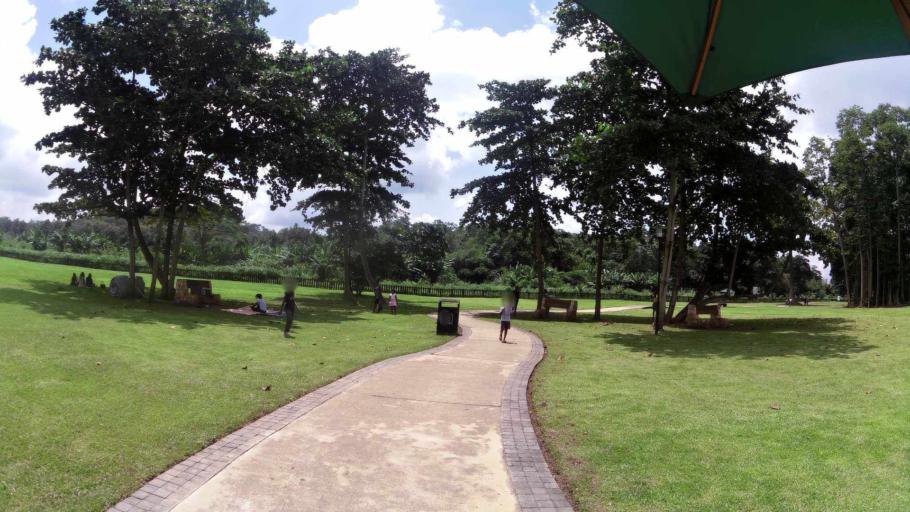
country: NG
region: Oyo
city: Ibadan
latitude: 7.4076
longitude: 3.9009
